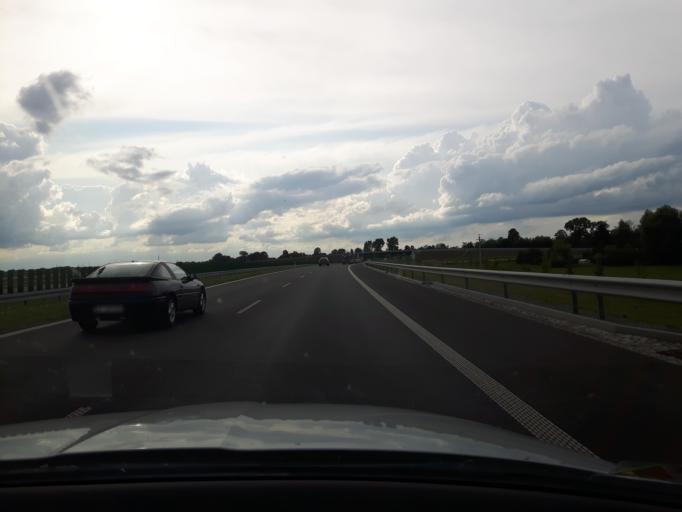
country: PL
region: Pomeranian Voivodeship
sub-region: Powiat nowodworski
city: Nowy Dwor Gdanski
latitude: 54.1744
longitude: 19.1961
